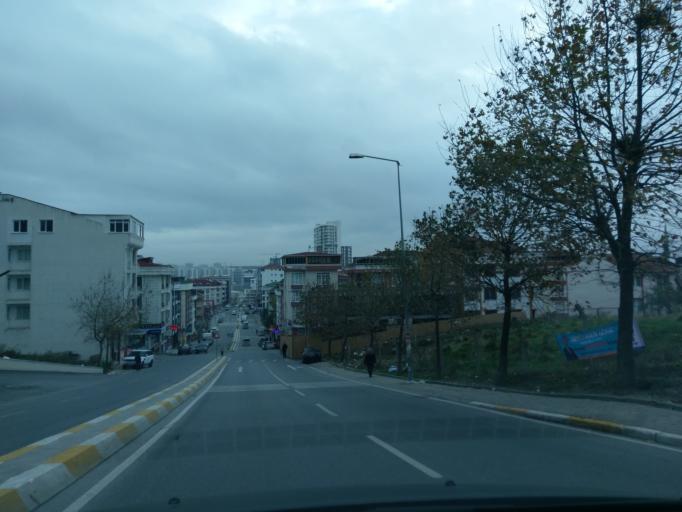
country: TR
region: Istanbul
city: Esenyurt
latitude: 41.0104
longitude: 28.6628
